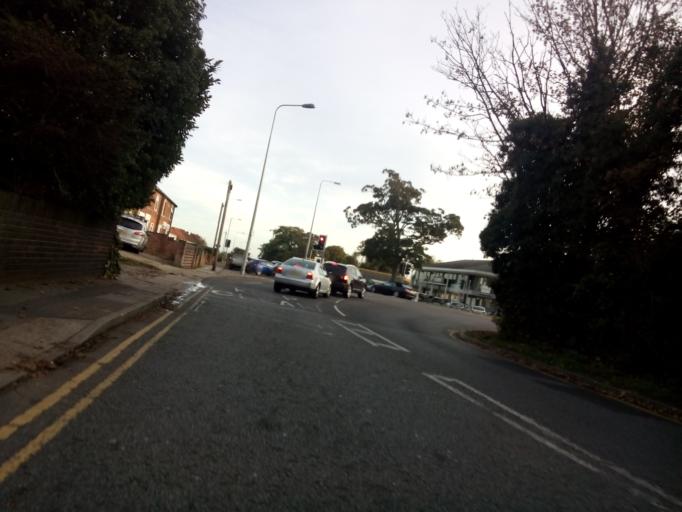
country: GB
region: England
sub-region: Suffolk
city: Bramford
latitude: 52.0817
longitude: 1.1245
